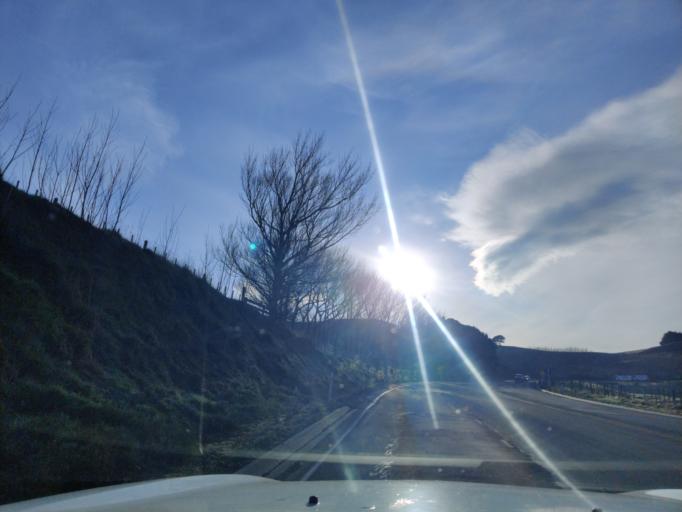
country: NZ
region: Manawatu-Wanganui
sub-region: Palmerston North City
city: Palmerston North
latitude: -40.2858
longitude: 175.7725
